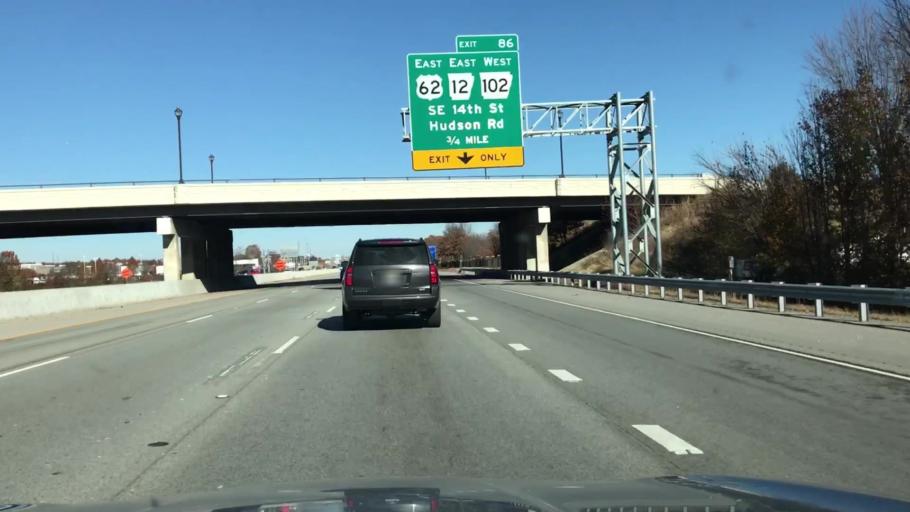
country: US
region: Arkansas
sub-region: Benton County
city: Bentonville
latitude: 36.3417
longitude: -94.1814
